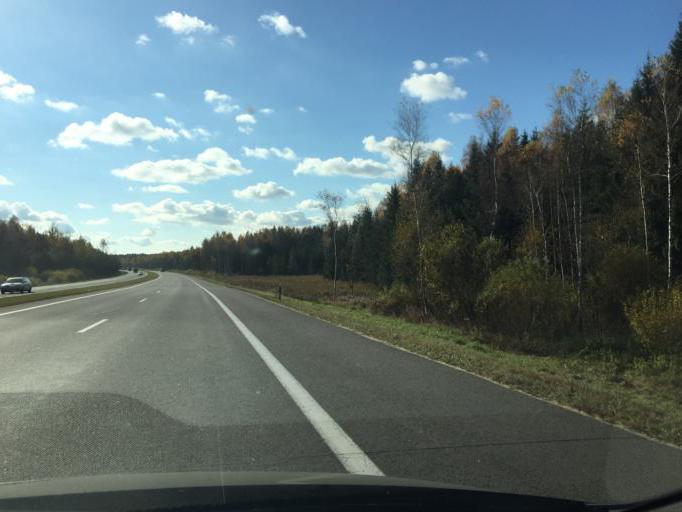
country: BY
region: Minsk
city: Slabada
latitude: 53.9419
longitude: 27.9675
